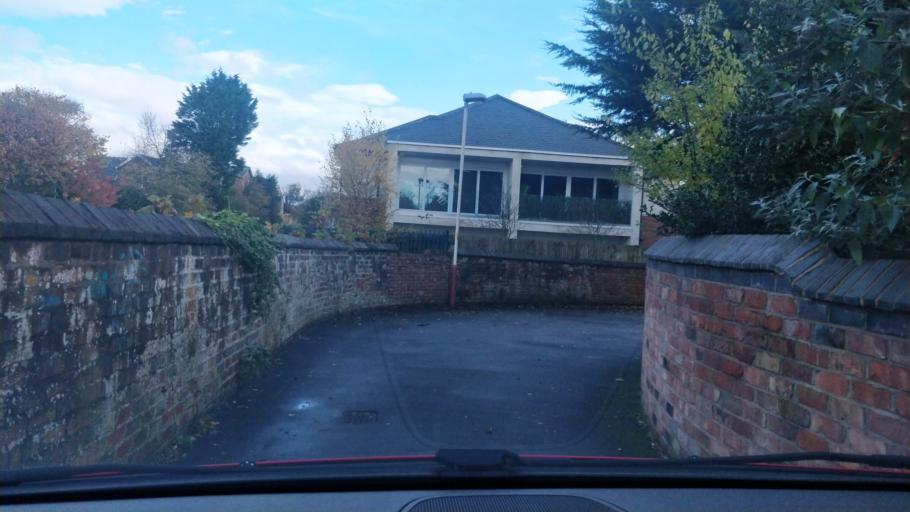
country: GB
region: England
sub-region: Sefton
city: Southport
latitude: 53.6314
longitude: -3.0166
